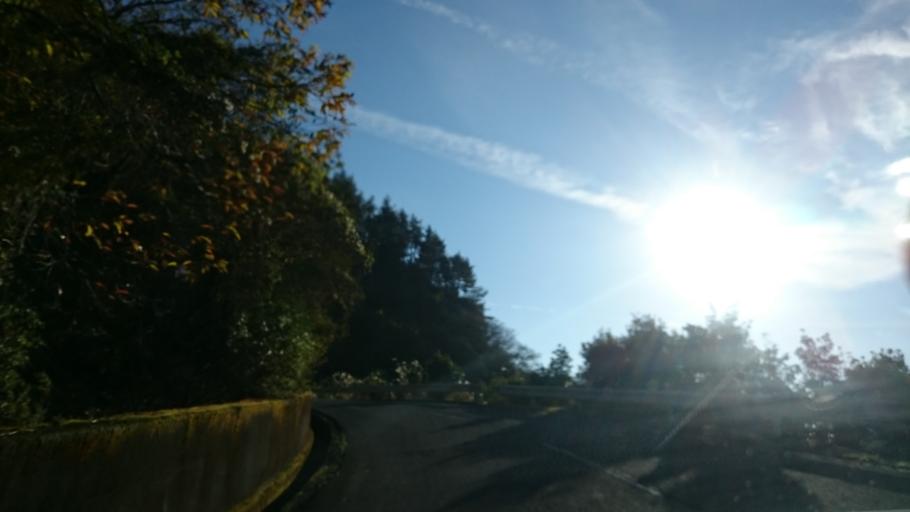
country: JP
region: Shizuoka
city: Heda
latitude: 34.9744
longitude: 138.8284
